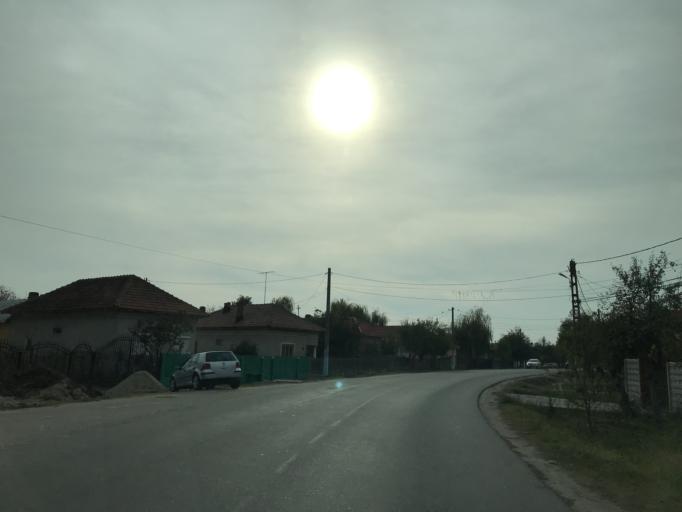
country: RO
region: Olt
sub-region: Comuna Piatra Olt
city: Piatra
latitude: 44.3701
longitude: 24.3125
